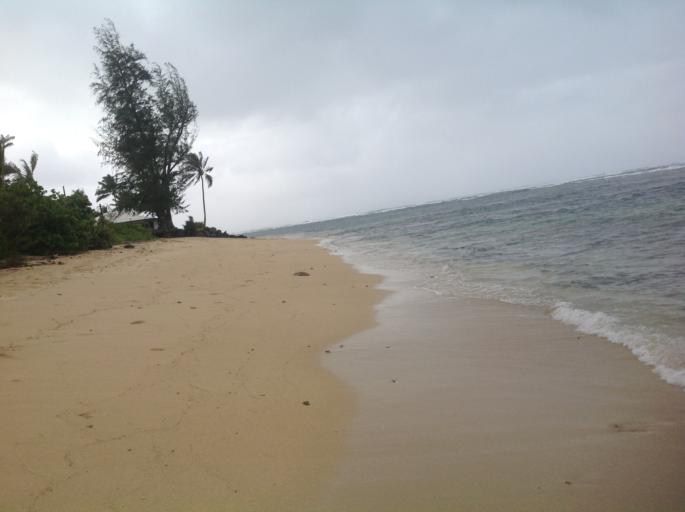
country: US
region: Hawaii
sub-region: Honolulu County
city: Waialua
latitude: 21.5833
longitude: -158.1344
